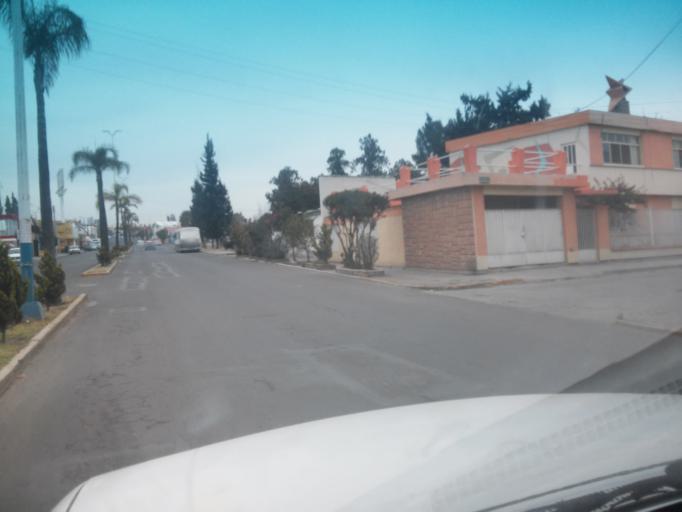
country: MX
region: Durango
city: Victoria de Durango
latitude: 24.0107
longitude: -104.6784
